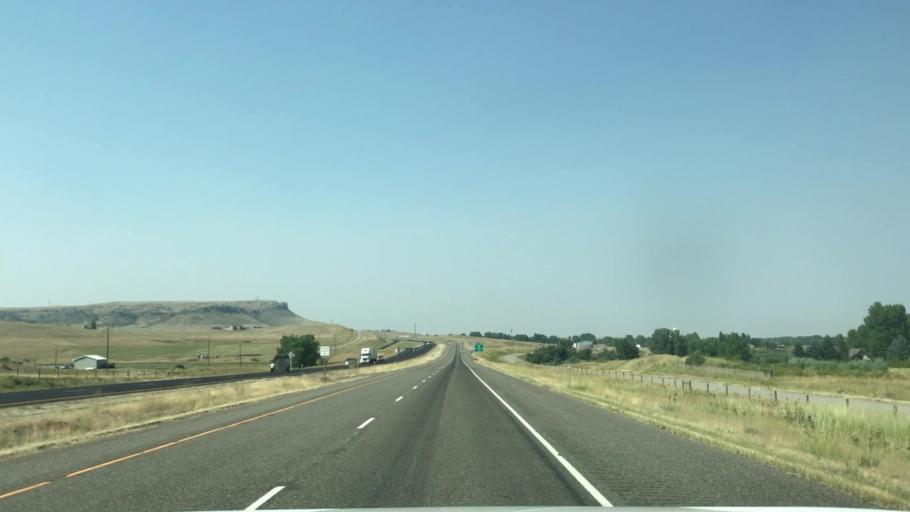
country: US
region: Montana
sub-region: Cascade County
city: Sun Prairie
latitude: 47.2528
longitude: -111.7099
